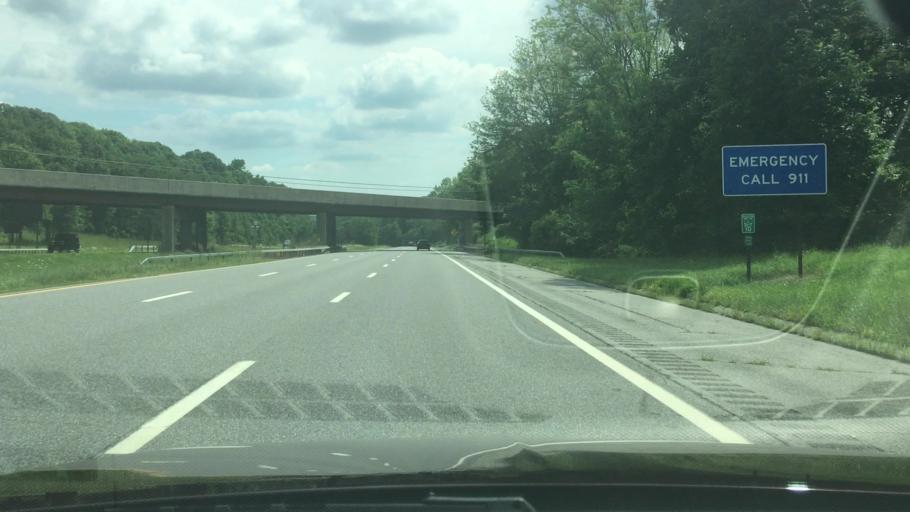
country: US
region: New York
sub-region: Westchester County
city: Briarcliff Manor
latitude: 41.2003
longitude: -73.8074
